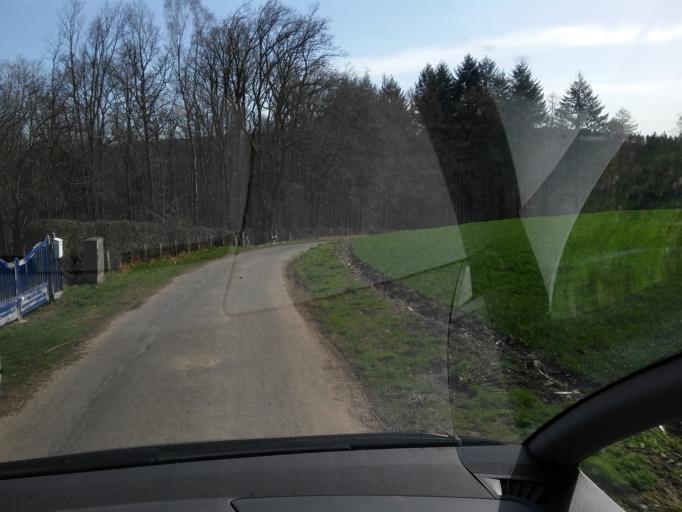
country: BE
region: Wallonia
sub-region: Province du Luxembourg
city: Daverdisse
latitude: 49.9956
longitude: 5.1497
